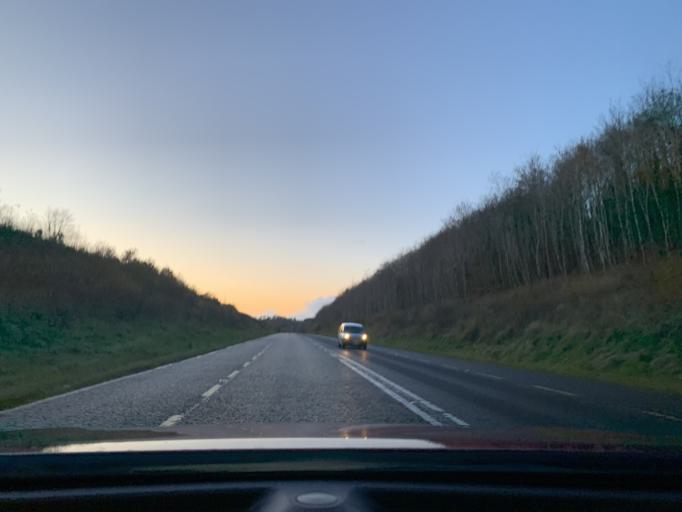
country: IE
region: Connaught
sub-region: County Leitrim
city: Carrick-on-Shannon
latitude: 53.9364
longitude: -8.0141
